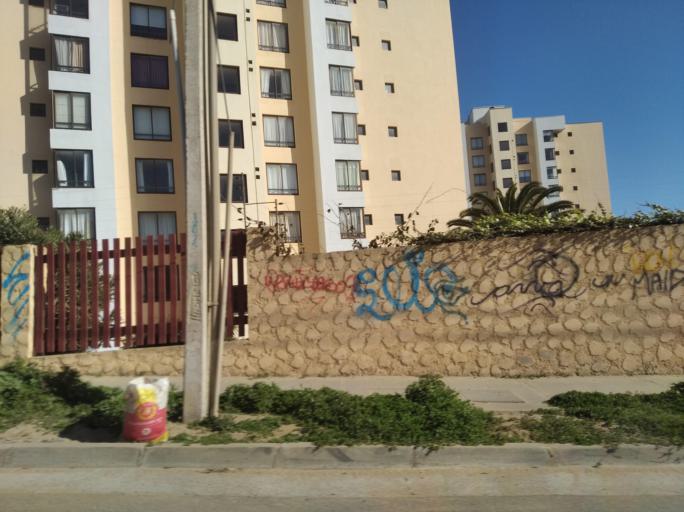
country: CL
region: Valparaiso
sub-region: San Antonio Province
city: El Tabo
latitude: -33.4580
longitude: -71.6627
